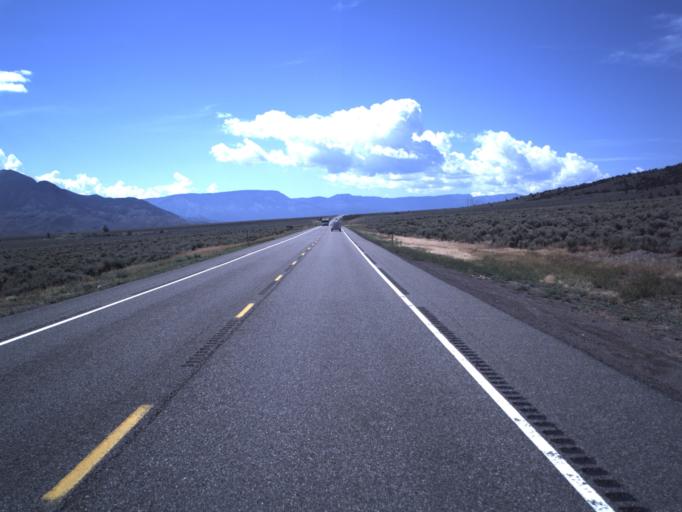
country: US
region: Utah
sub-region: Piute County
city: Junction
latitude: 38.3569
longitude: -112.2218
